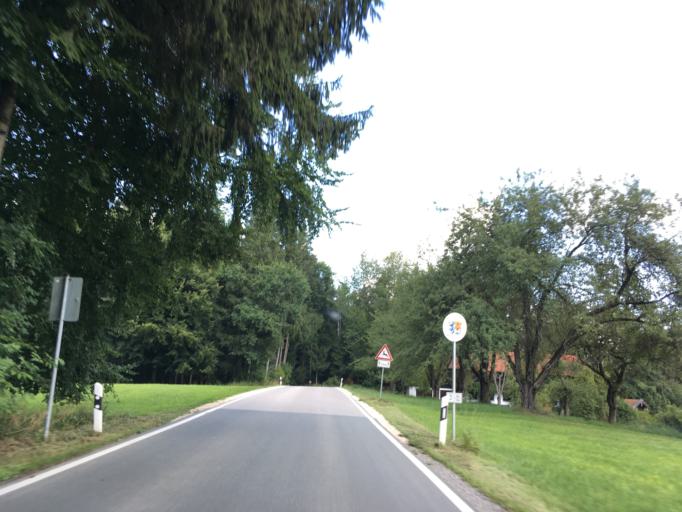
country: DE
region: Bavaria
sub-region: Upper Bavaria
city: Eggstatt
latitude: 47.9537
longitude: 12.3780
